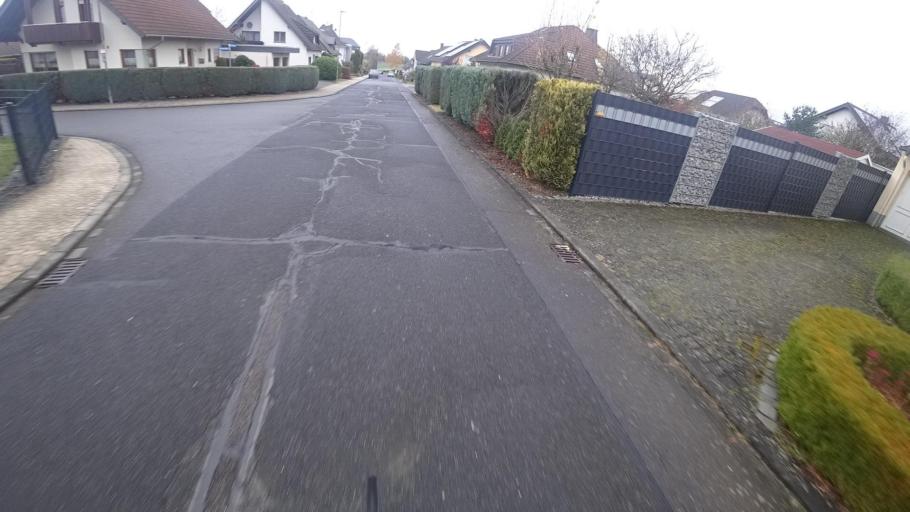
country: DE
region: Rheinland-Pfalz
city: Halsenbach
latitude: 50.1742
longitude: 7.5561
